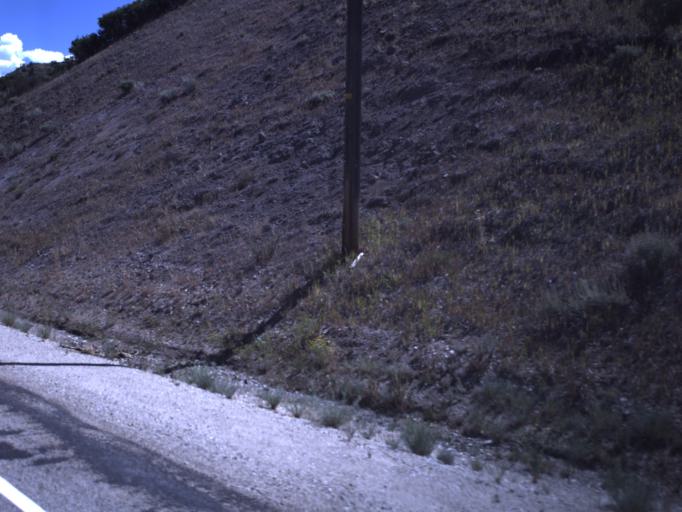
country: US
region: Utah
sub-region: Summit County
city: Francis
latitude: 40.5997
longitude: -111.3398
